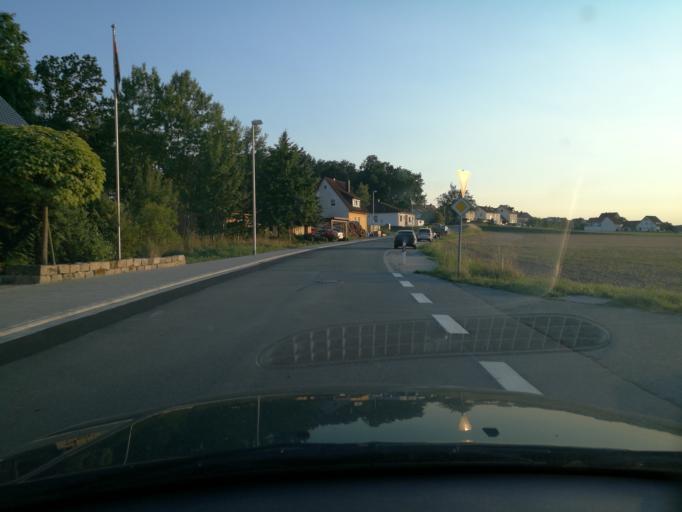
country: DE
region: Bavaria
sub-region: Regierungsbezirk Mittelfranken
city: Hessdorf
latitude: 49.6396
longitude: 10.9063
